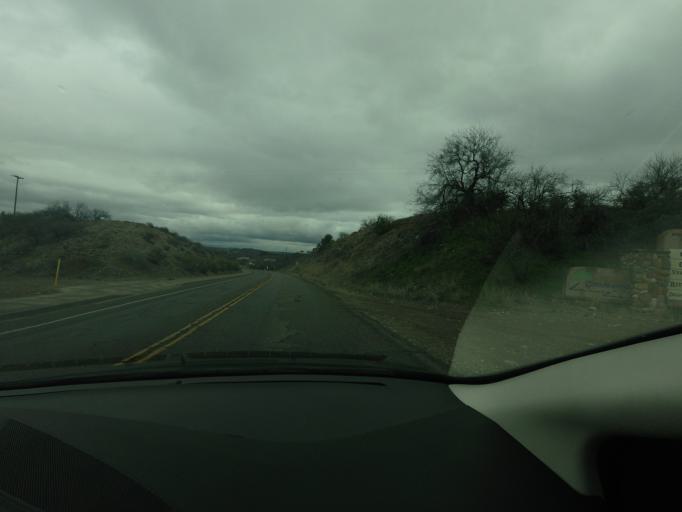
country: US
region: Arizona
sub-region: Yavapai County
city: Cottonwood
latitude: 34.7511
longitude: -112.0328
